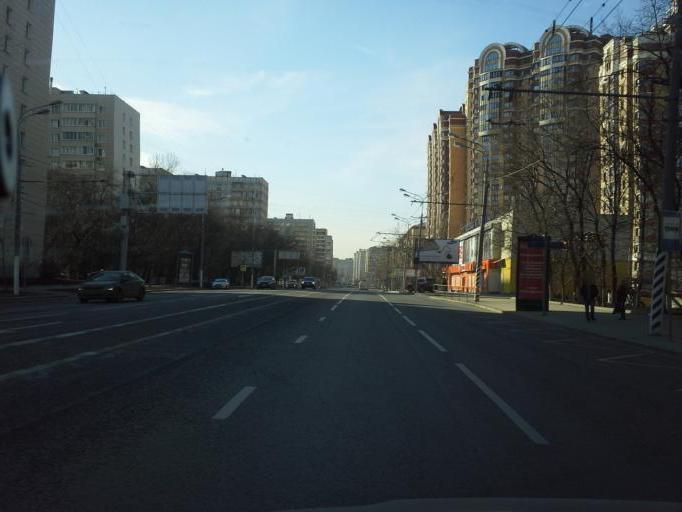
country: RU
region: Moscow
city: Taganskiy
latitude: 55.7379
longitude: 37.6835
